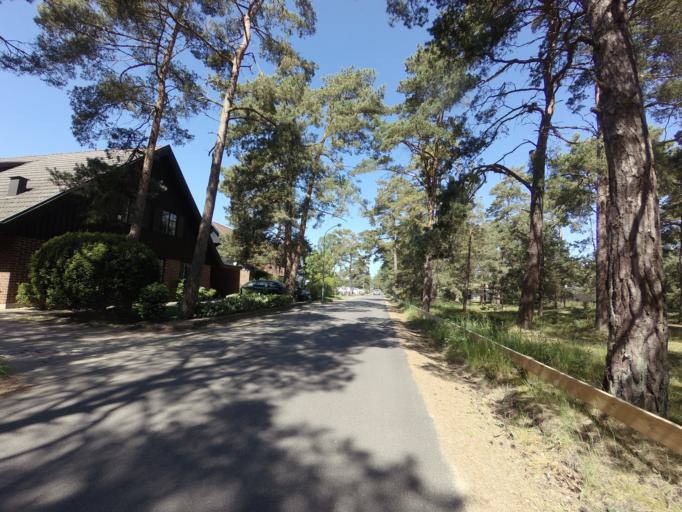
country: SE
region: Skane
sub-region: Vellinge Kommun
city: Hollviken
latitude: 55.4067
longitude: 12.9558
